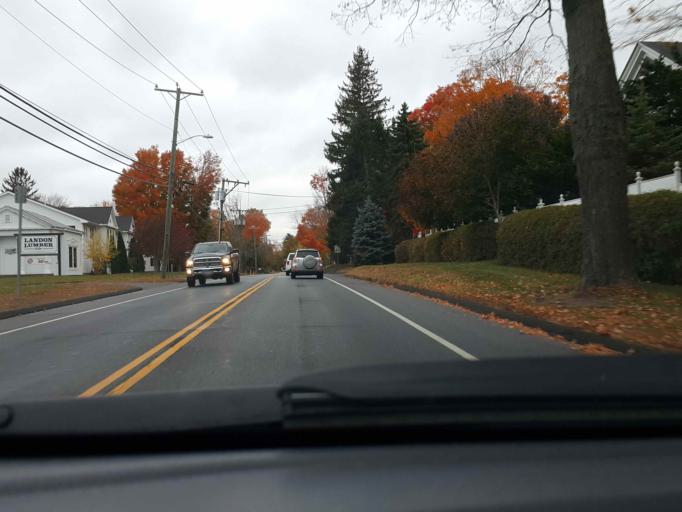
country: US
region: Connecticut
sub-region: New Haven County
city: Madison Center
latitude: 41.2838
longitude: -72.6349
